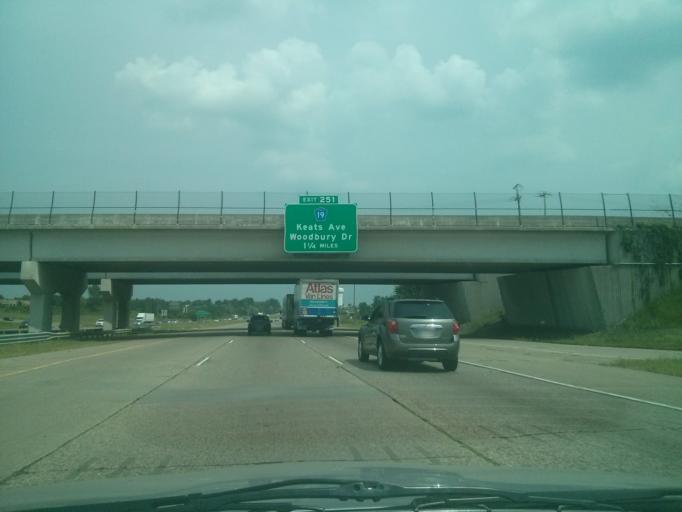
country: US
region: Minnesota
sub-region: Washington County
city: Oakdale
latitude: 44.9484
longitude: -92.9355
